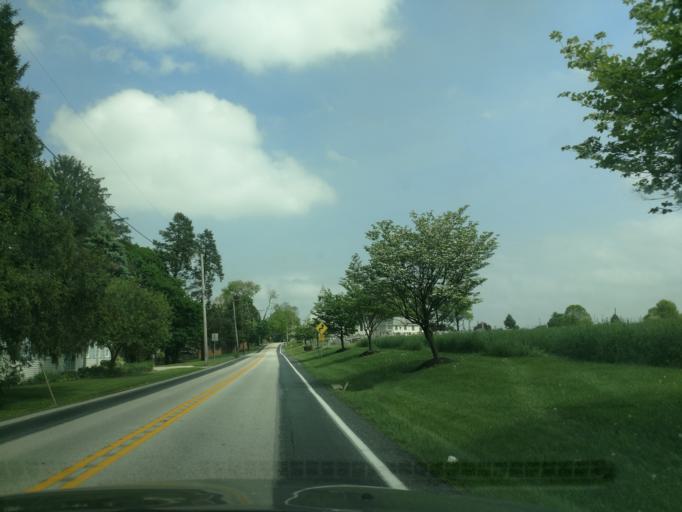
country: US
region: Pennsylvania
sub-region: Chester County
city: Kenilworth
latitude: 40.1770
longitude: -75.6274
